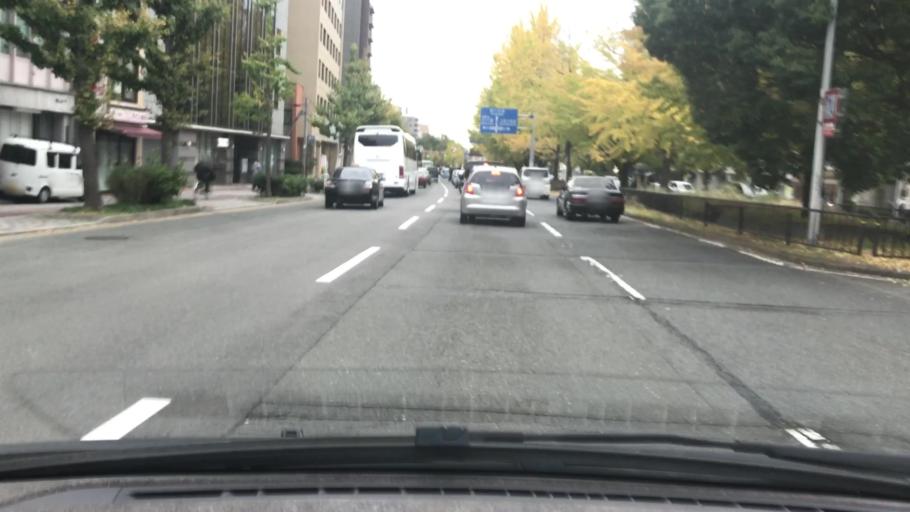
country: JP
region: Kyoto
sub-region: Kyoto-shi
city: Kamigyo-ku
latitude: 35.0315
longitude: 135.7520
